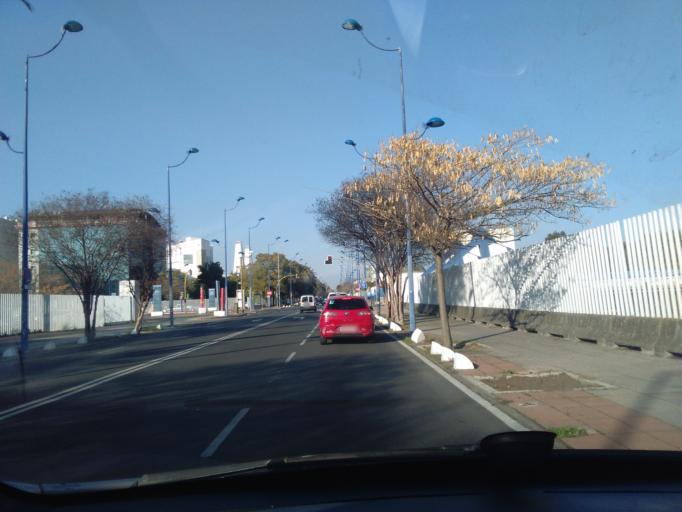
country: ES
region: Andalusia
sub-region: Provincia de Sevilla
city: Camas
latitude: 37.4049
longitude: -6.0034
